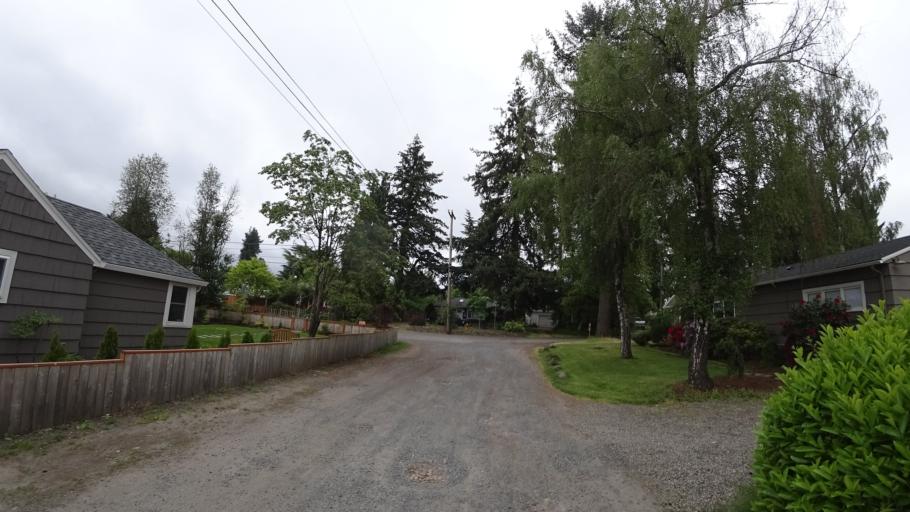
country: US
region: Oregon
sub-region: Multnomah County
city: Portland
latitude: 45.5528
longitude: -122.6096
